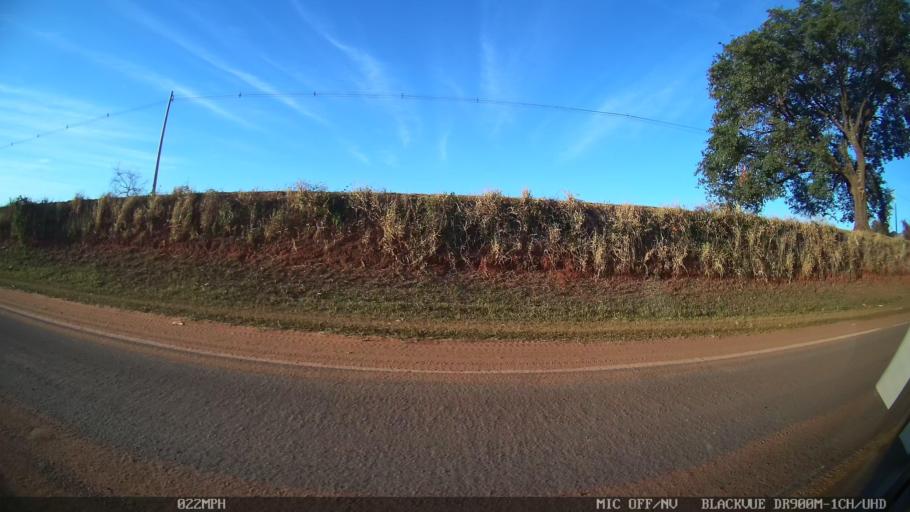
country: BR
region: Sao Paulo
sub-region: Catanduva
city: Catanduva
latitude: -21.0327
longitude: -49.1506
